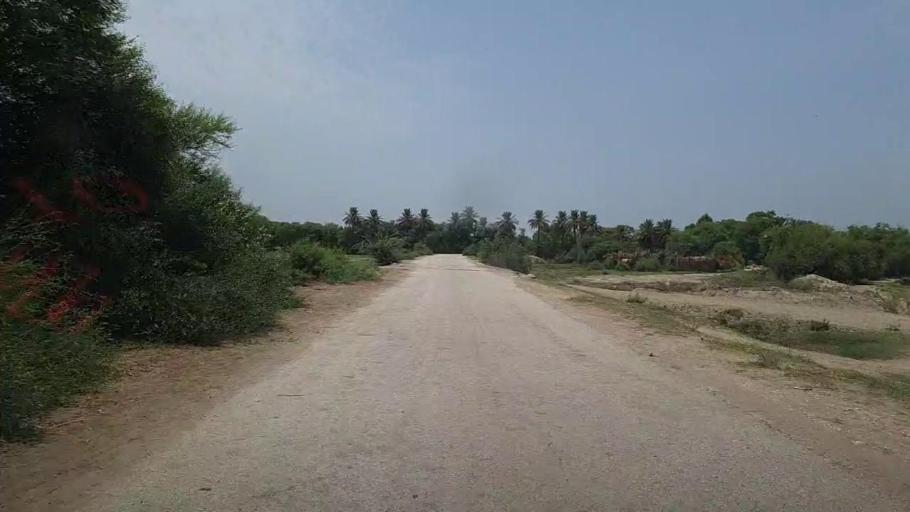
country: PK
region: Sindh
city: Pano Aqil
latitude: 27.8152
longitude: 69.2360
